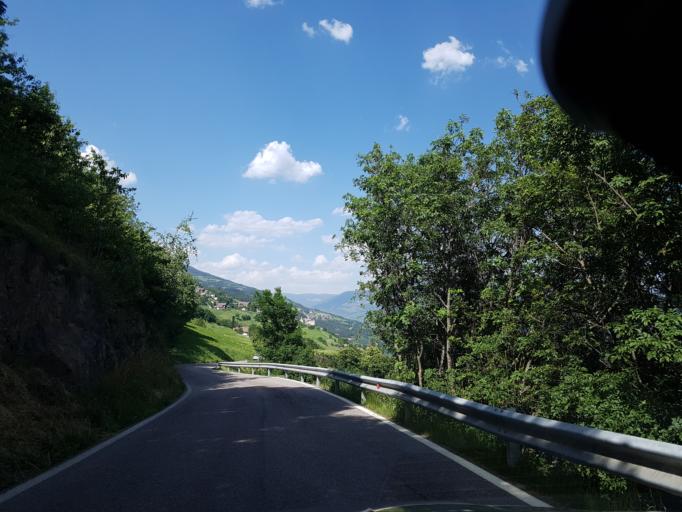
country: IT
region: Trentino-Alto Adige
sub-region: Bolzano
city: Villandro - Villanders
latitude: 46.6313
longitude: 11.5337
